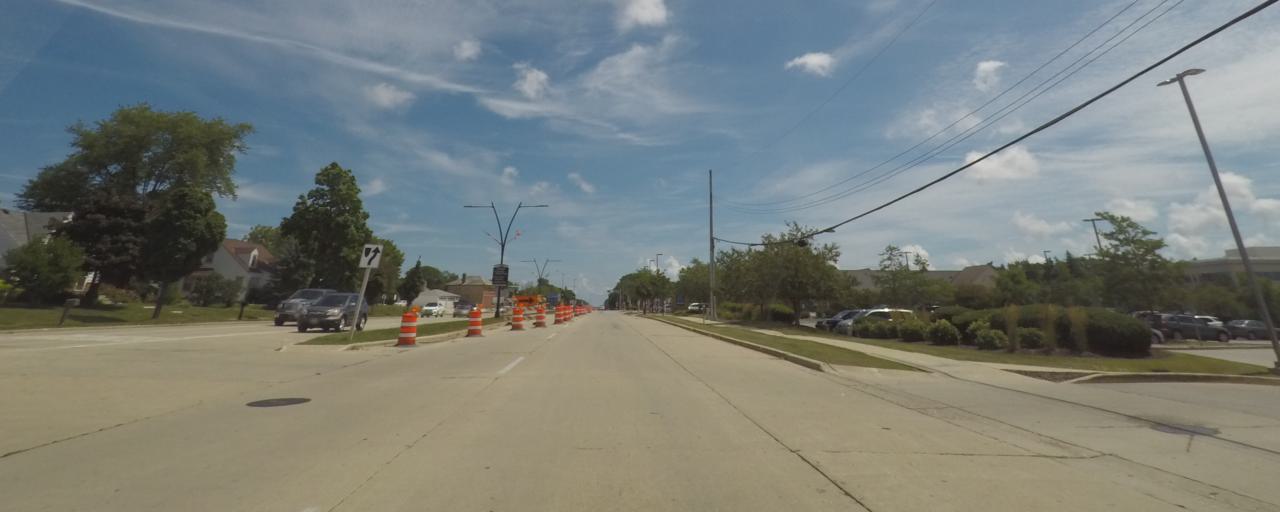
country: US
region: Wisconsin
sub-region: Milwaukee County
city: Greendale
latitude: 42.9594
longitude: -87.9724
